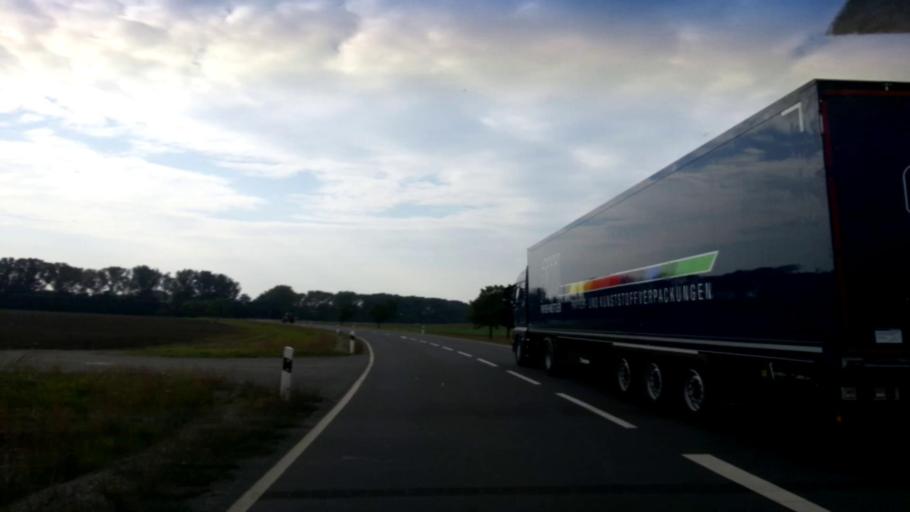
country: DE
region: Bavaria
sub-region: Regierungsbezirk Unterfranken
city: Sulzheim
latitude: 49.9432
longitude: 10.3713
